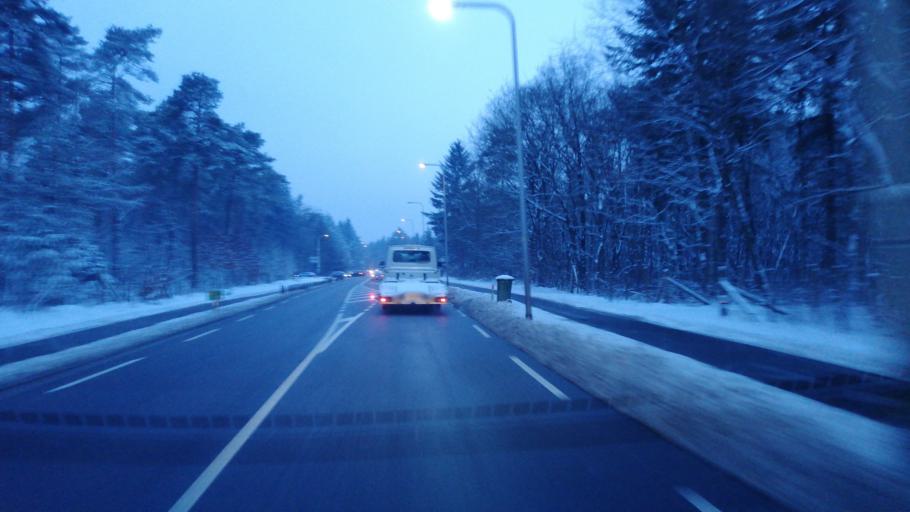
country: NL
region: Gelderland
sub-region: Gemeente Apeldoorn
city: Loenen
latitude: 52.1388
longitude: 5.9942
